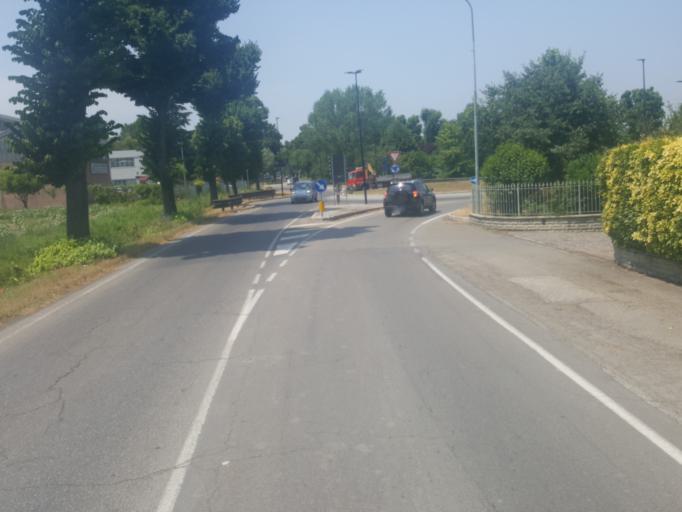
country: IT
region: Emilia-Romagna
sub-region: Provincia di Modena
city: Castelfranco Emilia
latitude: 44.5876
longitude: 11.0739
